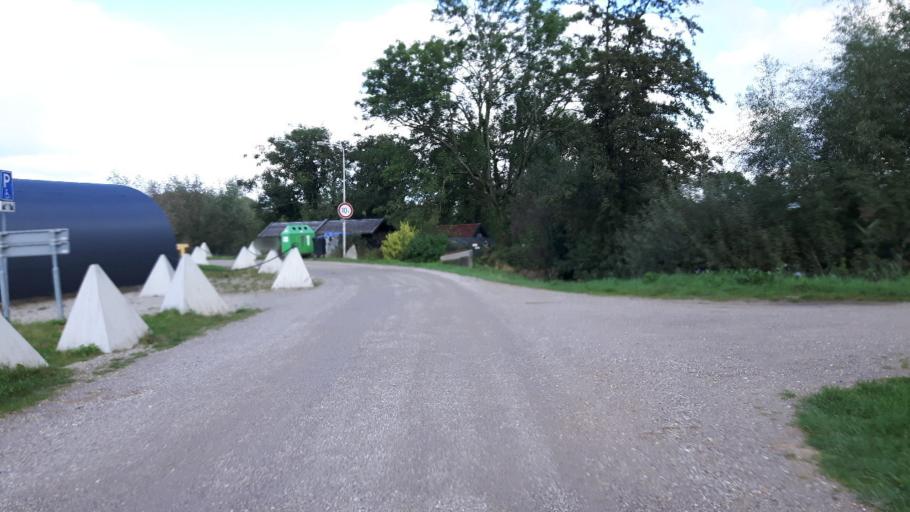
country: NL
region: South Holland
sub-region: Gemeente Leerdam
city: Leerdam
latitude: 51.8773
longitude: 5.1202
